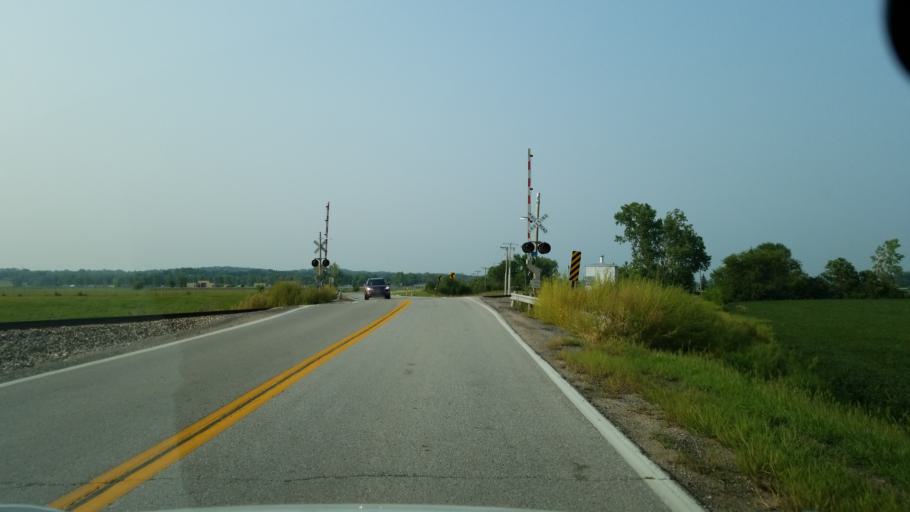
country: US
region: Nebraska
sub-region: Sarpy County
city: Bellevue
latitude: 41.1098
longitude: -95.8899
